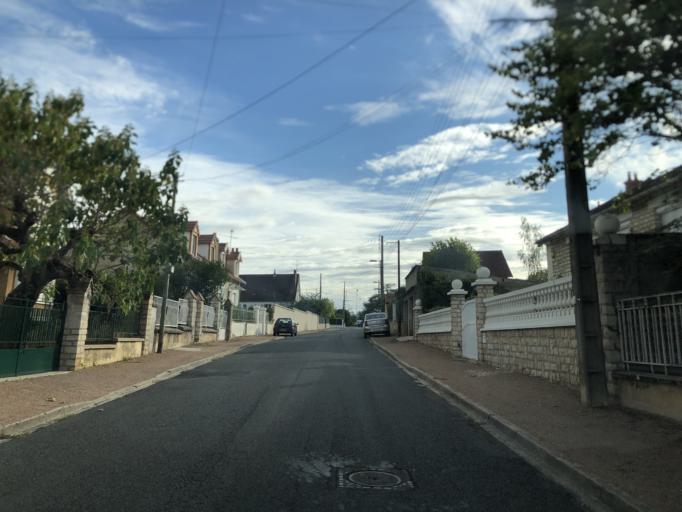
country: FR
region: Bourgogne
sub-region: Departement de l'Yonne
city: Auxerre
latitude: 47.7937
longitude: 3.5557
